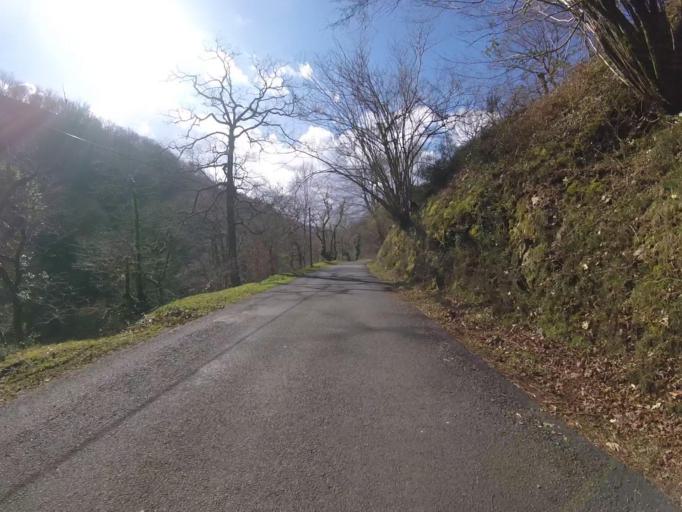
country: ES
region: Navarre
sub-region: Provincia de Navarra
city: Etxalar
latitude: 43.2684
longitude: -1.6043
